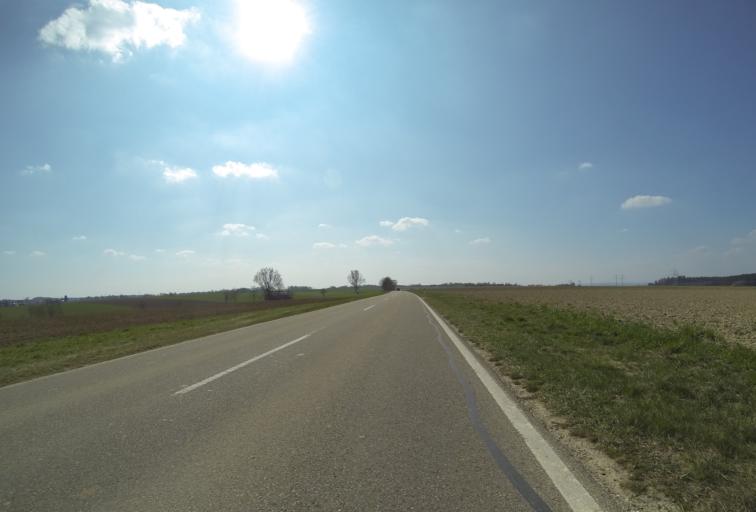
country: DE
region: Baden-Wuerttemberg
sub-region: Tuebingen Region
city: Staig
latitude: 48.2998
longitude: 9.9707
